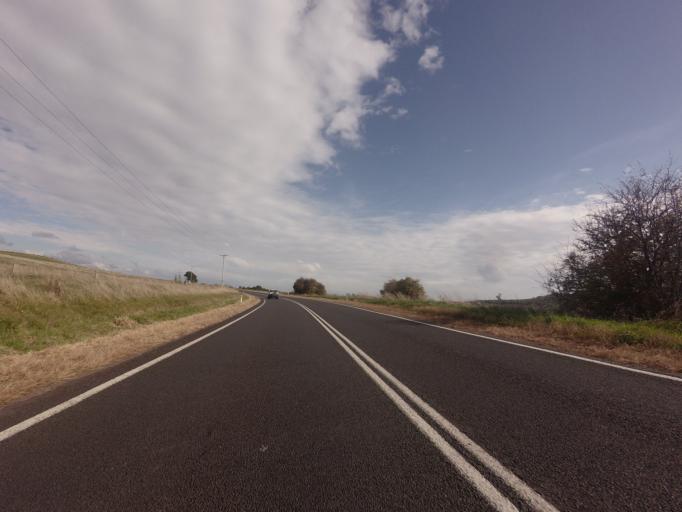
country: AU
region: Tasmania
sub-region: Meander Valley
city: Deloraine
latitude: -41.5181
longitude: 146.7235
